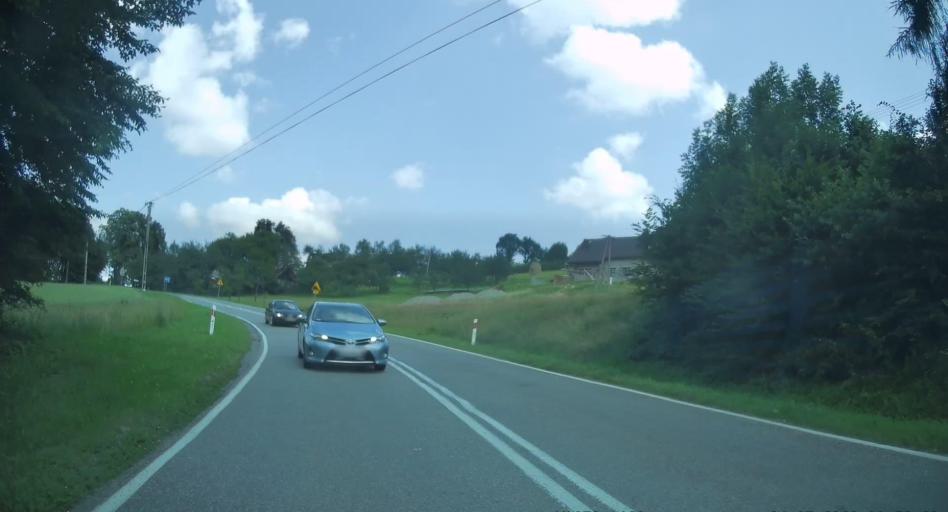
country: PL
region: Lesser Poland Voivodeship
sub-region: Powiat tarnowski
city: Zakliczyn
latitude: 49.7666
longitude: 20.7814
